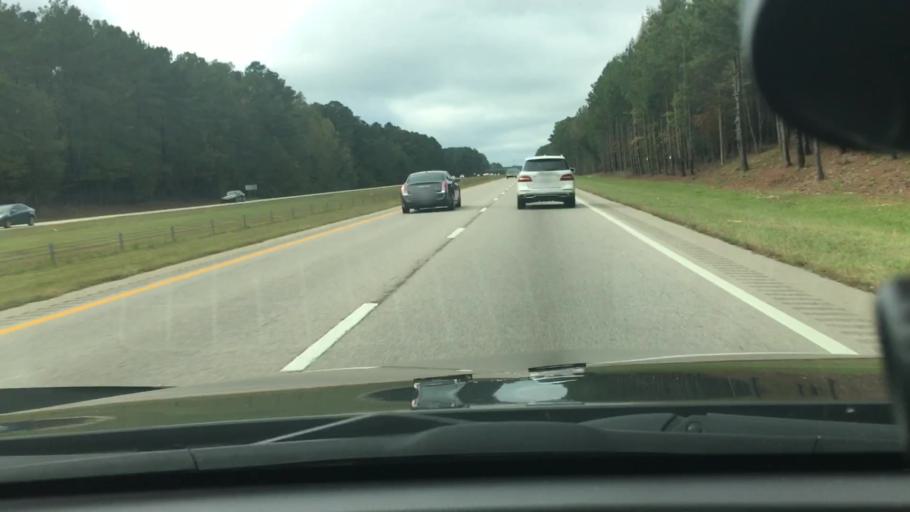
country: US
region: North Carolina
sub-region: Wake County
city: Zebulon
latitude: 35.8186
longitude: -78.2589
